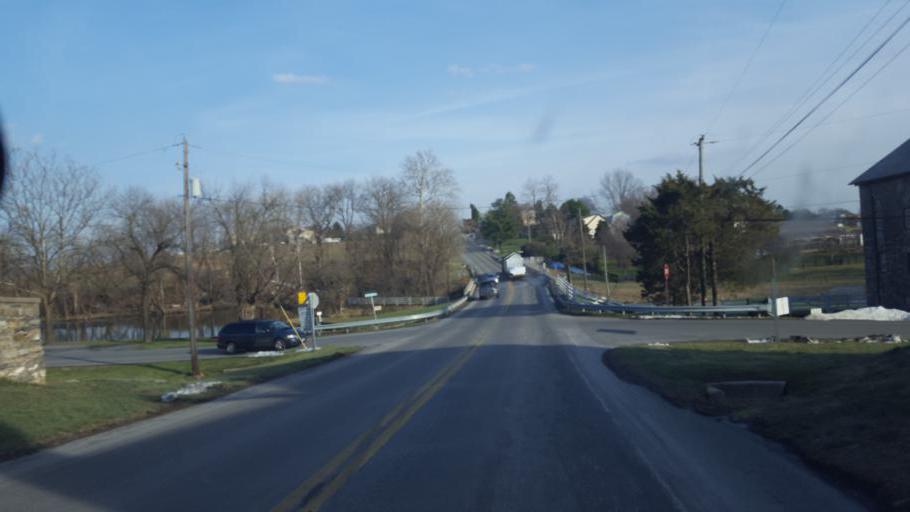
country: US
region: Pennsylvania
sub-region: Lancaster County
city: Intercourse
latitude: 40.0633
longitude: -76.1574
